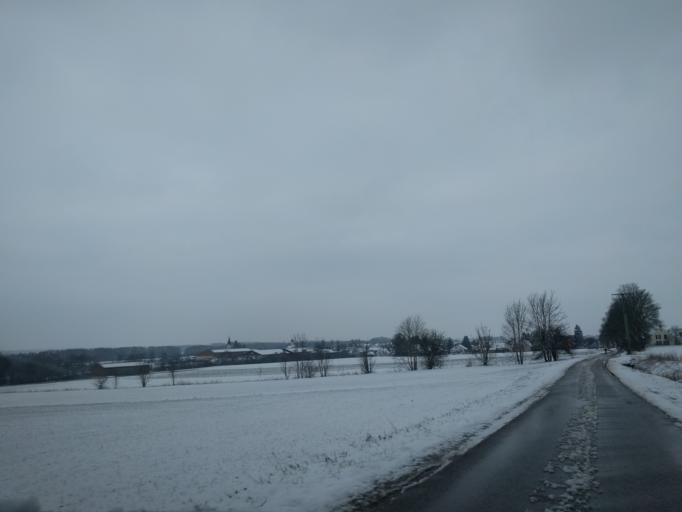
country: DE
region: Bavaria
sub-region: Swabia
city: Tapfheim
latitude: 48.6888
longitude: 10.7153
